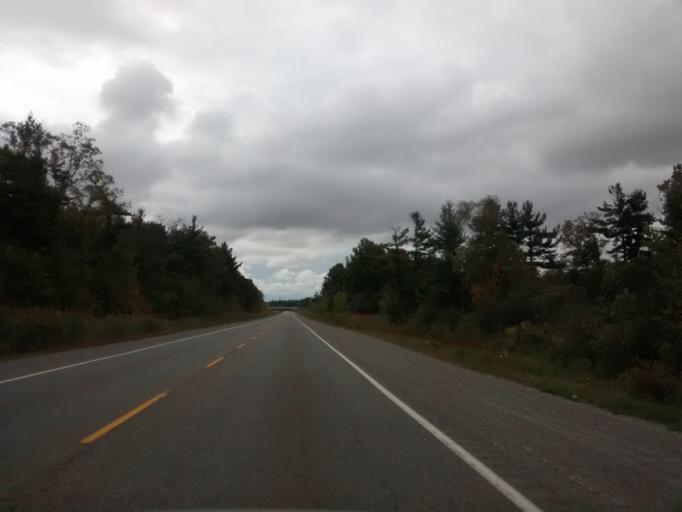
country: CA
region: Ontario
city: Ancaster
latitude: 43.1785
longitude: -79.9636
